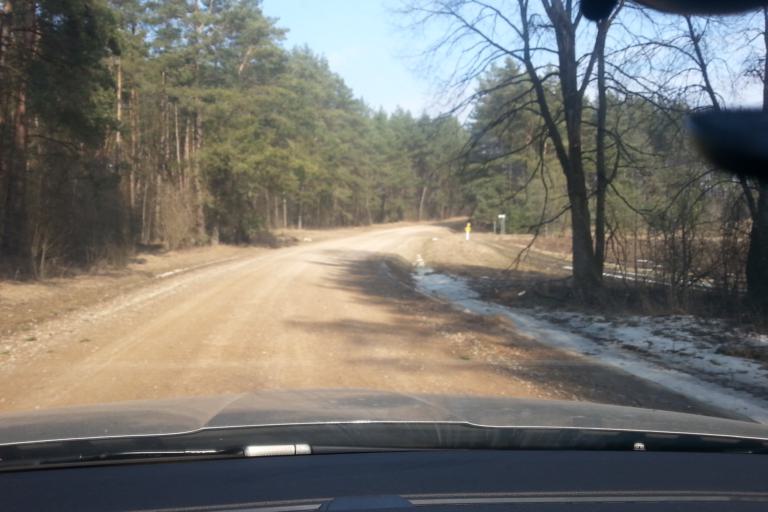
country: LT
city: Trakai
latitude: 54.5801
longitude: 24.9735
